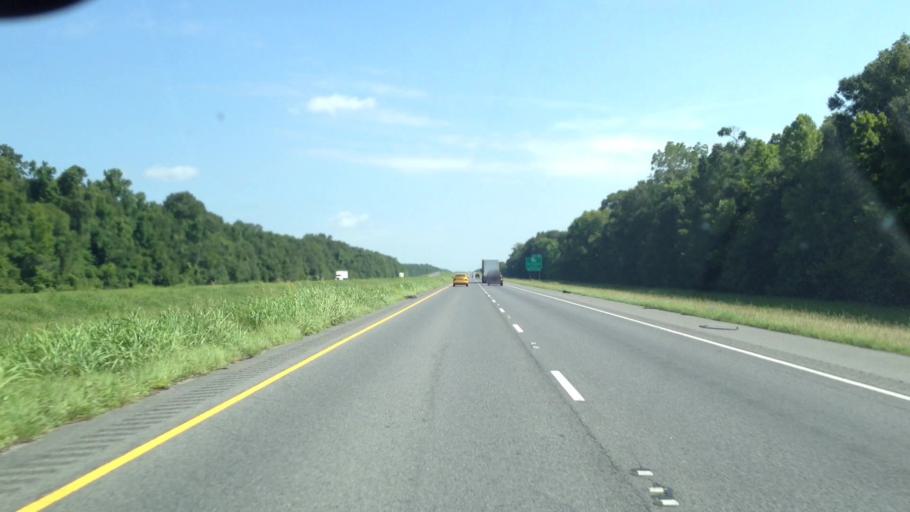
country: US
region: Louisiana
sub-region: Avoyelles Parish
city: Bunkie
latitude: 30.8506
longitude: -92.2284
